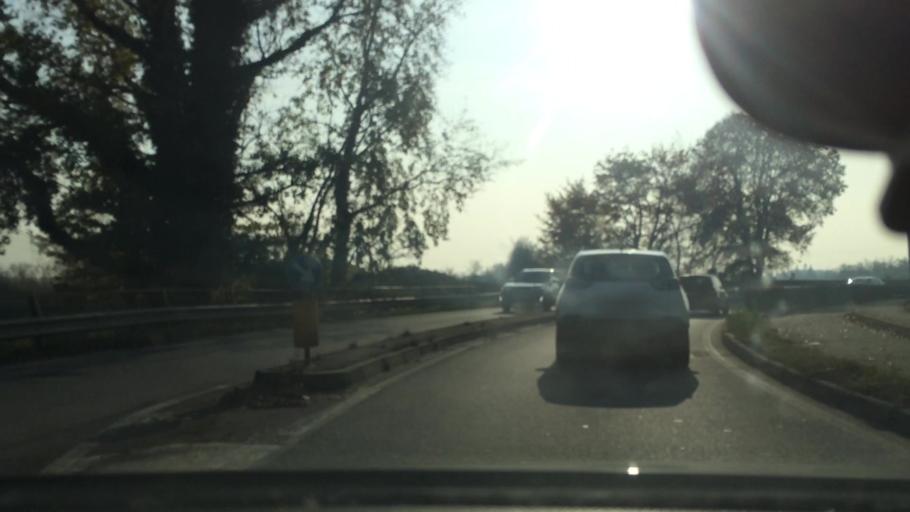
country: IT
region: Lombardy
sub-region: Citta metropolitana di Milano
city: Passirana
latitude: 45.5470
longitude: 9.0494
